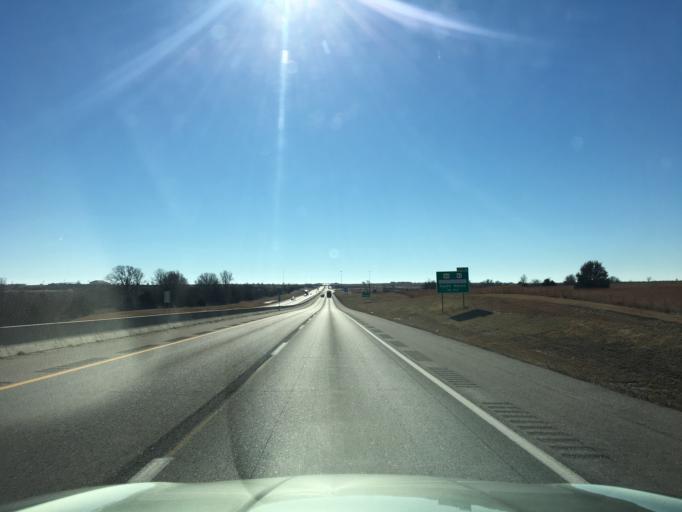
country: US
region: Kansas
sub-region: Sumner County
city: Wellington
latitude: 37.0691
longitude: -97.3385
